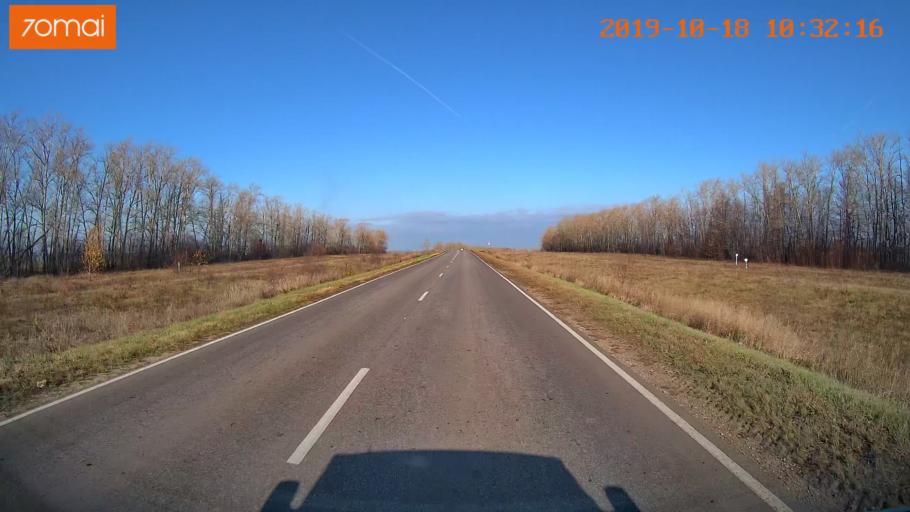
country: RU
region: Tula
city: Kurkino
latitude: 53.4917
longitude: 38.6247
